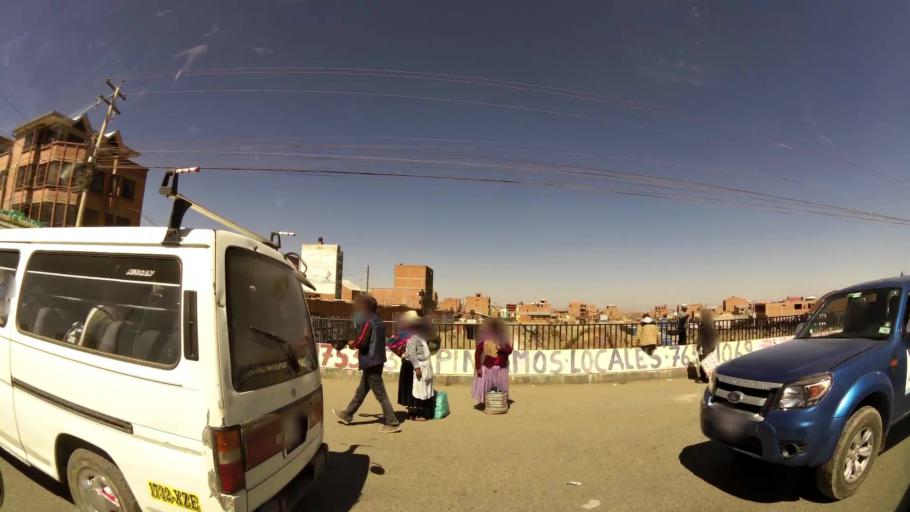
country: BO
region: La Paz
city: La Paz
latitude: -16.4913
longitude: -68.2024
